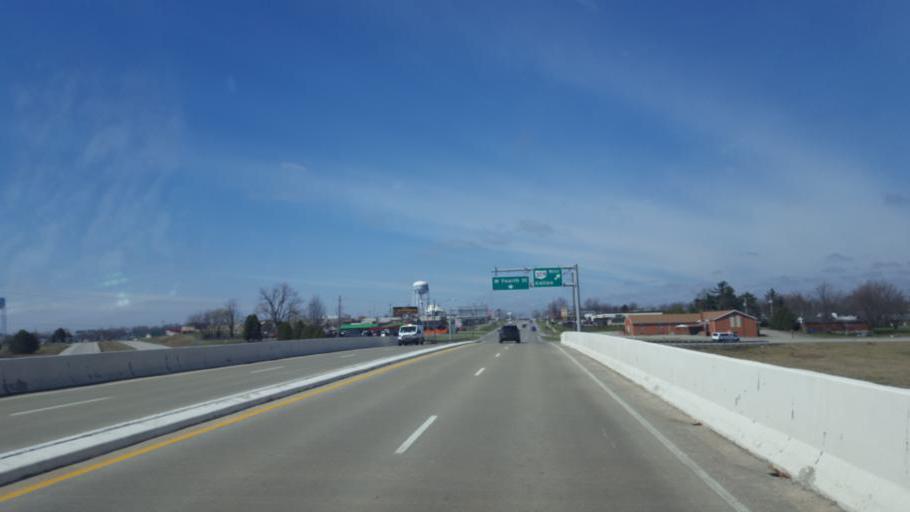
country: US
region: Ohio
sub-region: Richland County
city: Ontario
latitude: 40.7711
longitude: -82.5817
